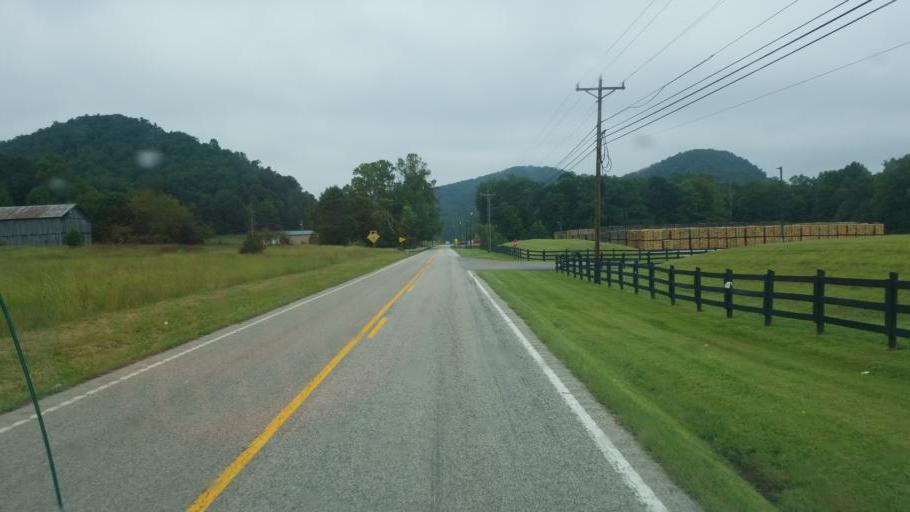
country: US
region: Kentucky
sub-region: Rowan County
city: Morehead
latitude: 38.2579
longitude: -83.4377
